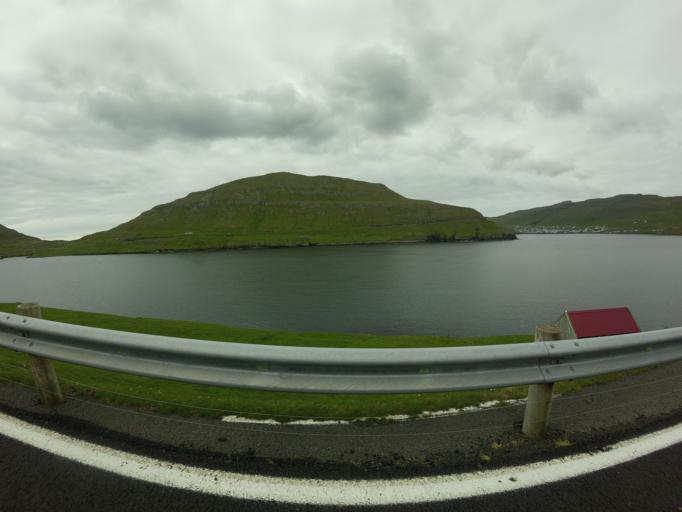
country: FO
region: Suduroy
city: Vagur
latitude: 61.4528
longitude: -6.7641
